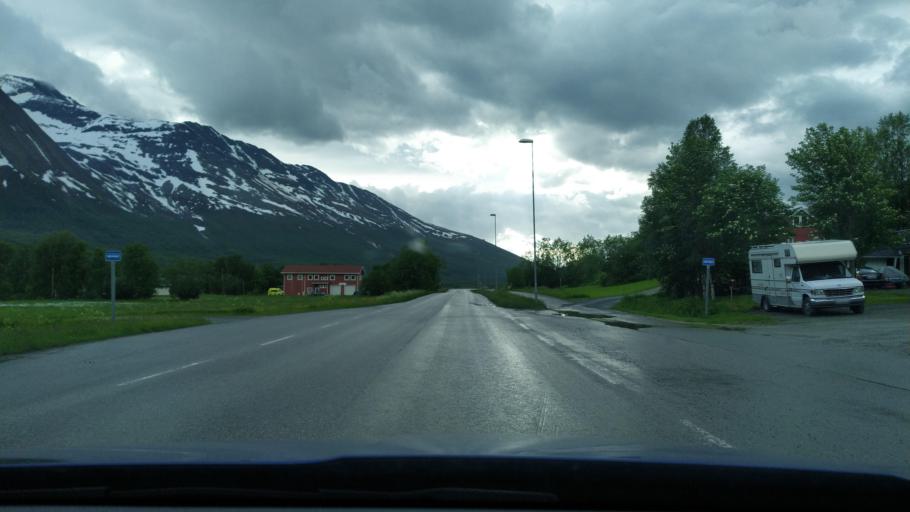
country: NO
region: Troms
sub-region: Balsfjord
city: Storsteinnes
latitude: 69.2200
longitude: 19.5452
